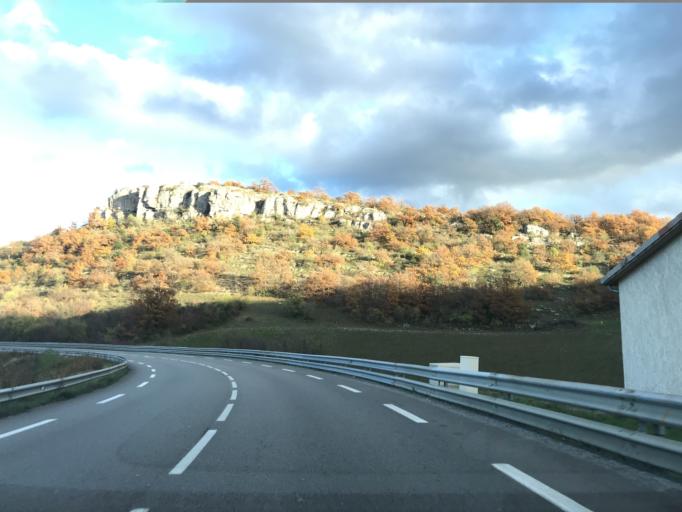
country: FR
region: Rhone-Alpes
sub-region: Departement de l'Ardeche
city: Alissas
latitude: 44.7100
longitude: 4.6236
